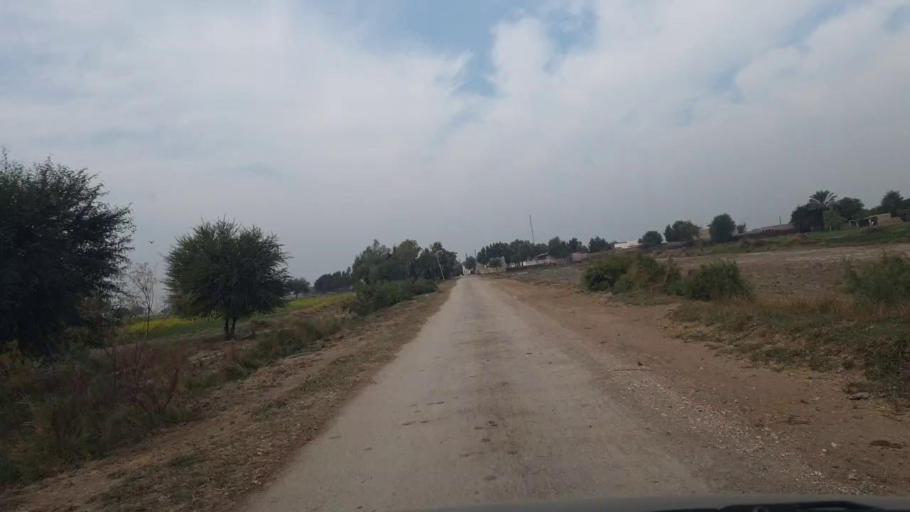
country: PK
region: Sindh
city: Shahdadpur
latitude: 25.9406
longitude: 68.6756
